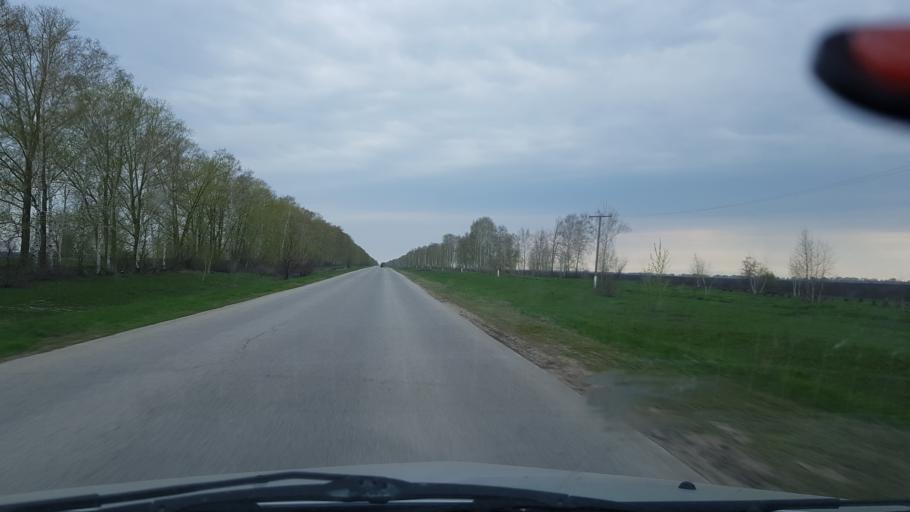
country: RU
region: Samara
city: Tol'yatti
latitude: 53.6586
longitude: 49.2382
